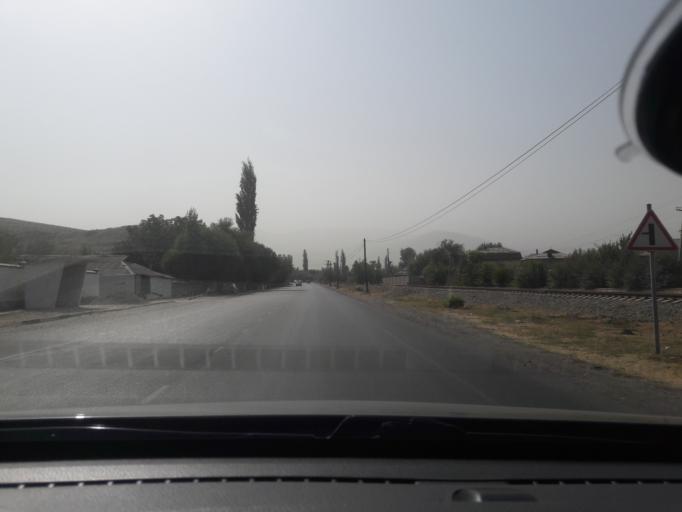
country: TJ
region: Republican Subordination
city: Vahdat
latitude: 38.5227
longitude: 69.0282
